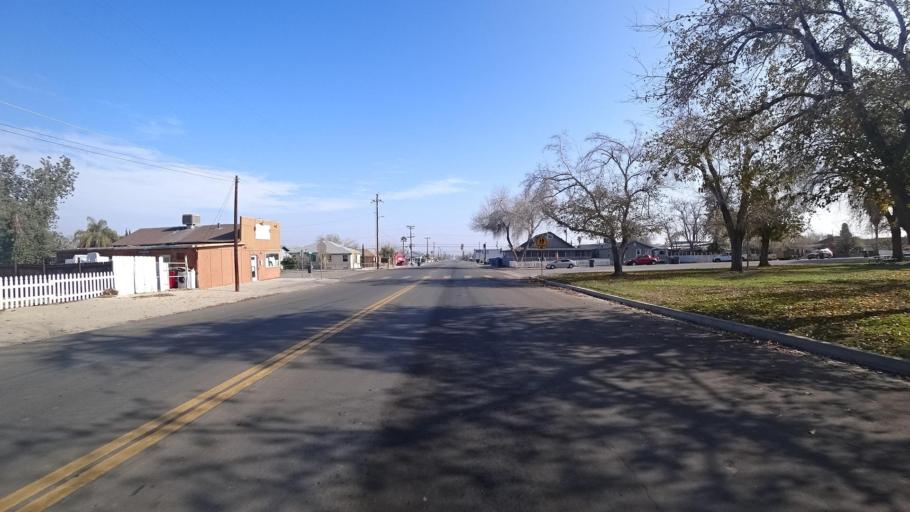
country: US
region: California
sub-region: Kern County
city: Ford City
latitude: 35.1545
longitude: -119.4581
